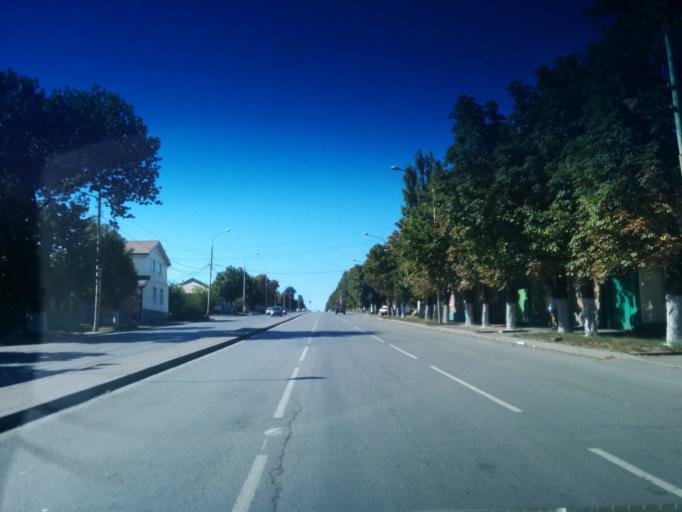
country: RU
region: Rostov
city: Shakhty
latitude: 47.6997
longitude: 40.2344
